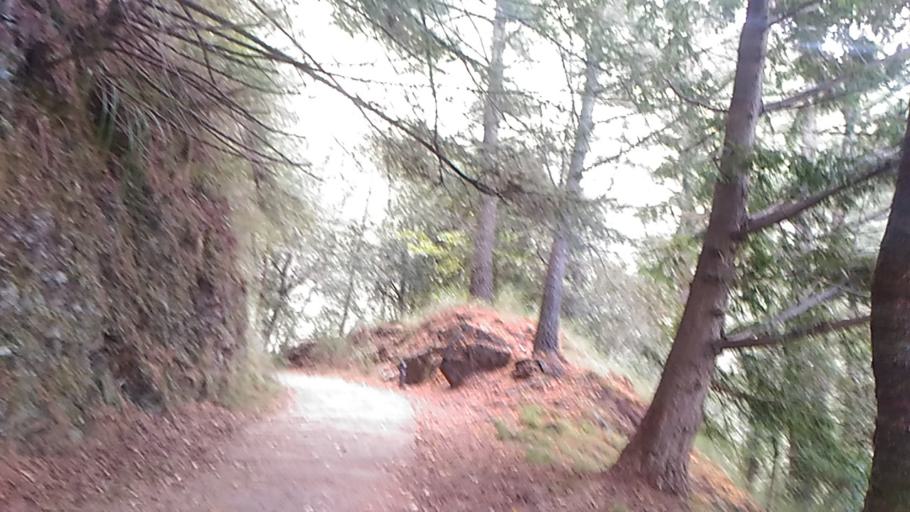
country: TW
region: Taiwan
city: Daxi
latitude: 24.4107
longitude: 121.3030
